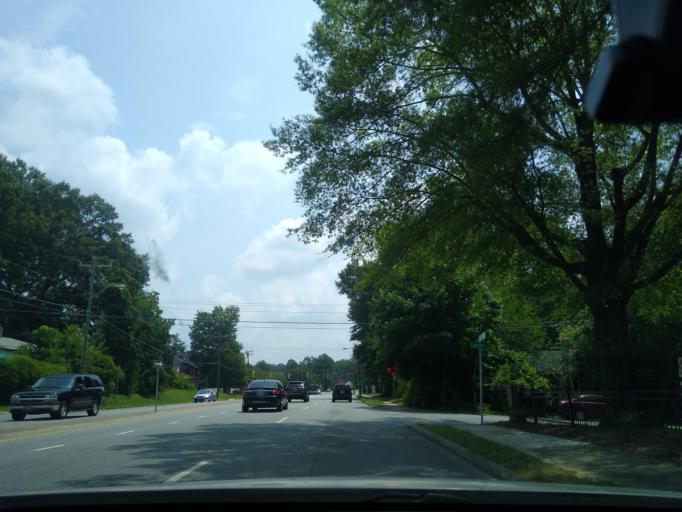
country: US
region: North Carolina
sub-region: Guilford County
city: Greensboro
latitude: 36.0644
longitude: -79.7727
